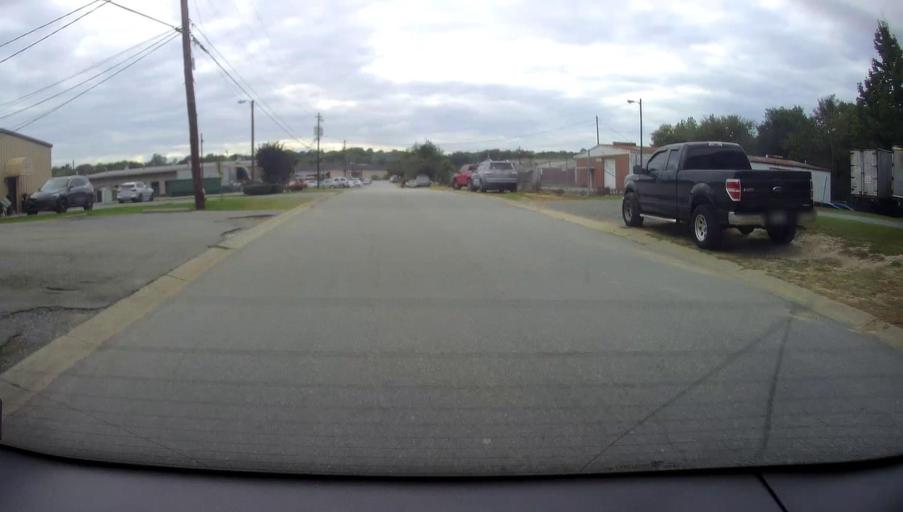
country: US
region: Georgia
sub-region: Bibb County
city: Macon
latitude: 32.8131
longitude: -83.6297
